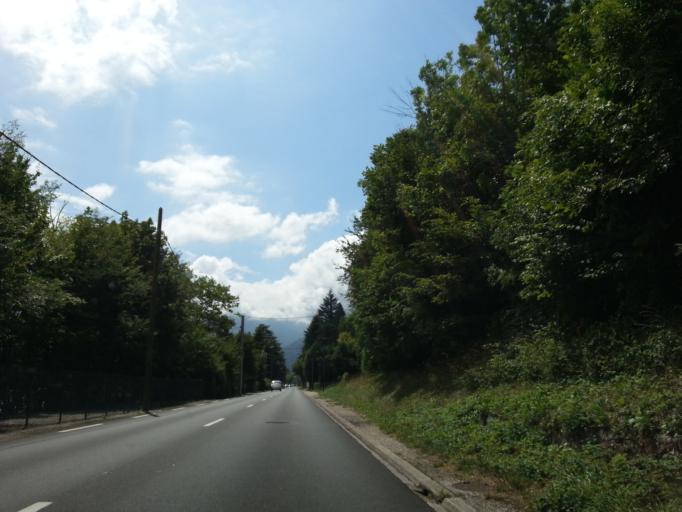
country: FR
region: Rhone-Alpes
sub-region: Departement de la Haute-Savoie
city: Doussard
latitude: 45.8023
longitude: 6.2123
